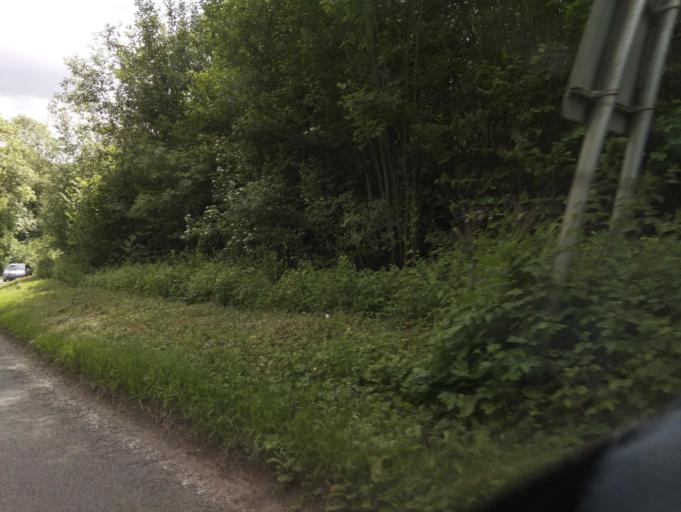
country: GB
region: England
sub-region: Herefordshire
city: Yatton
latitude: 51.9631
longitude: -2.5267
